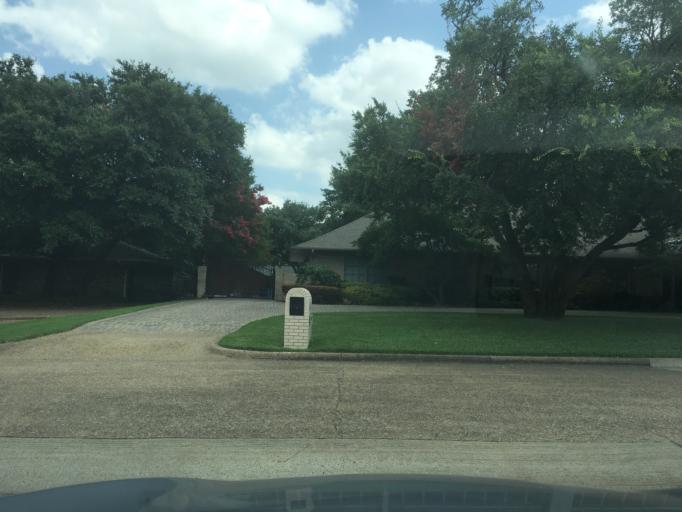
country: US
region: Texas
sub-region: Dallas County
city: University Park
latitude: 32.9001
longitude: -96.8140
